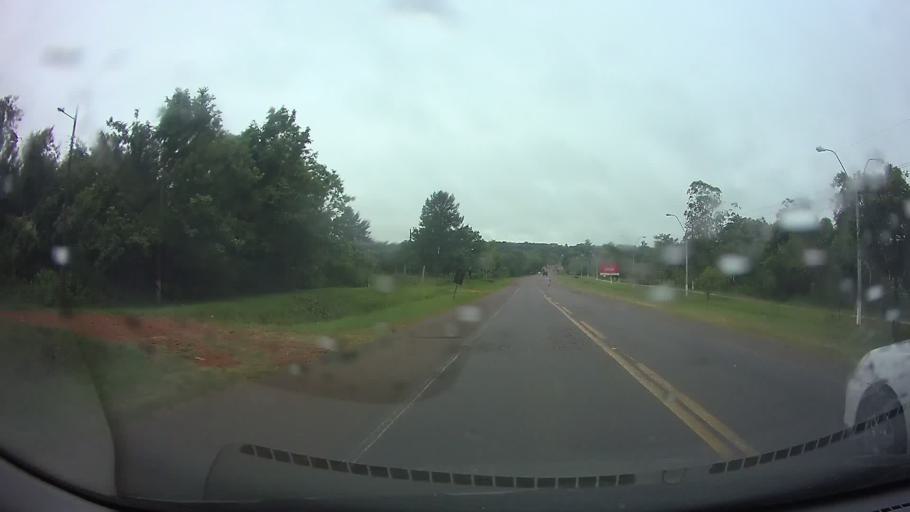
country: PY
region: Central
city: Ita
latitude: -25.5392
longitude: -57.3201
